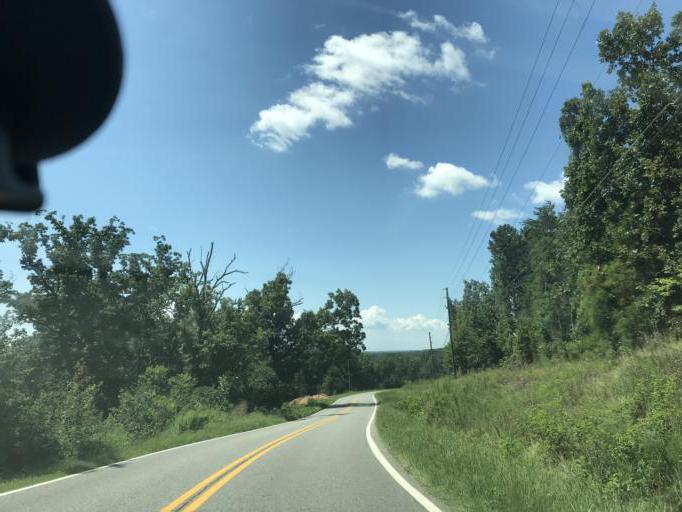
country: US
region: Georgia
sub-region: Forsyth County
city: Cumming
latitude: 34.3040
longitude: -84.0284
